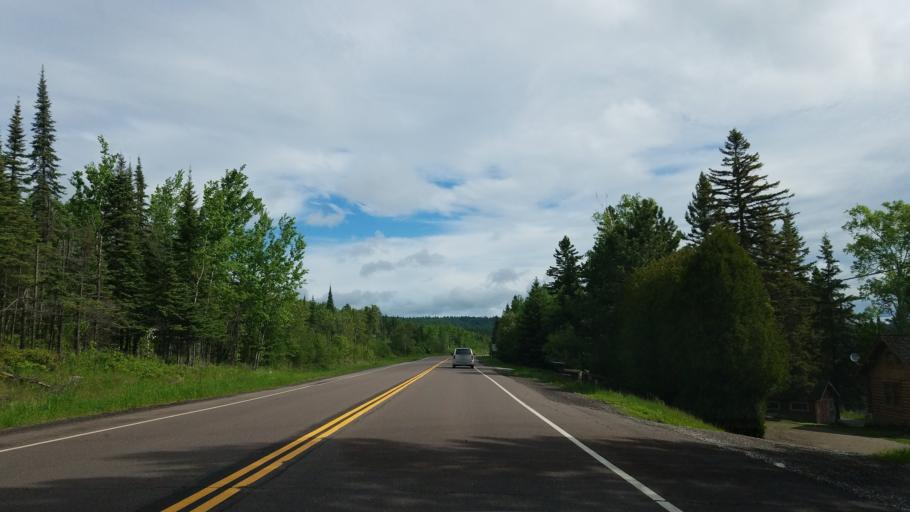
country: US
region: Minnesota
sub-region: Lake County
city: Two Harbors
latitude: 47.0772
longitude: -91.5861
